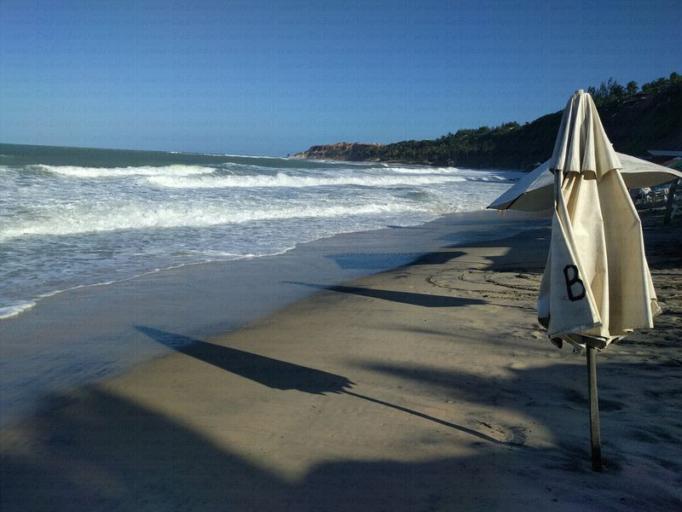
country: BR
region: Rio Grande do Norte
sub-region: Ares
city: Ares
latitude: -6.2304
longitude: -35.0422
